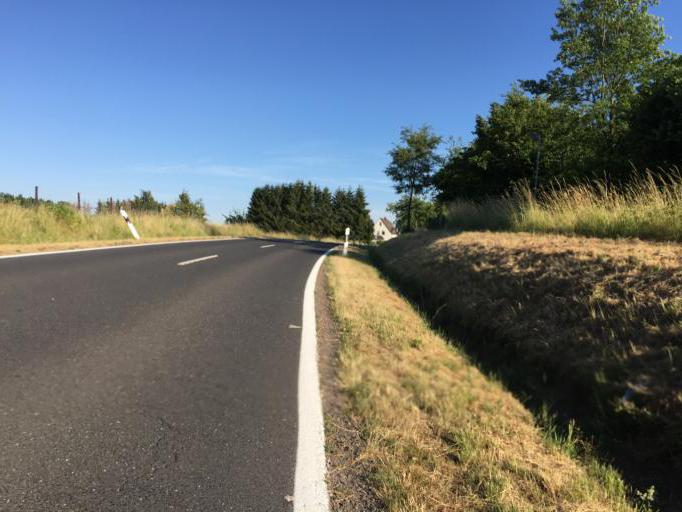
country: DE
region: Rheinland-Pfalz
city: Kaden
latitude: 50.5431
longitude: 7.9141
